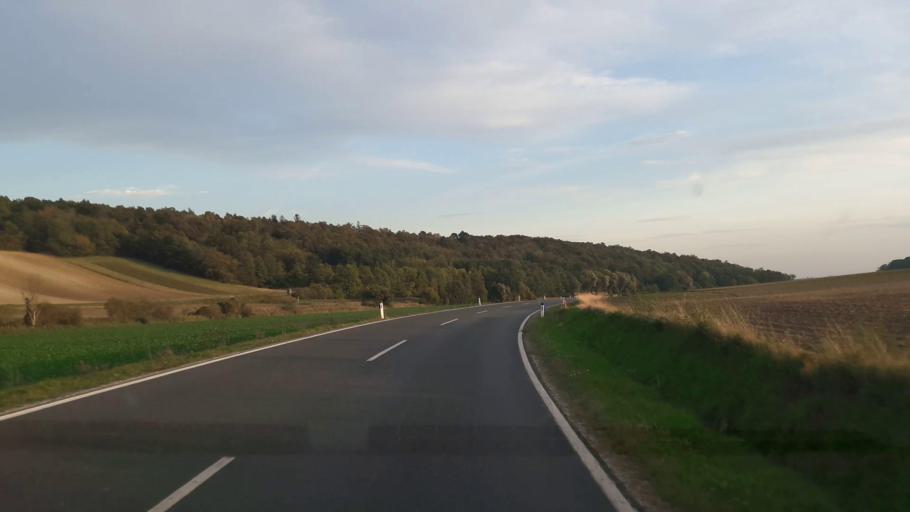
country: AT
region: Lower Austria
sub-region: Politischer Bezirk Korneuburg
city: Ernstbrunn
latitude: 48.4949
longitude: 16.3669
